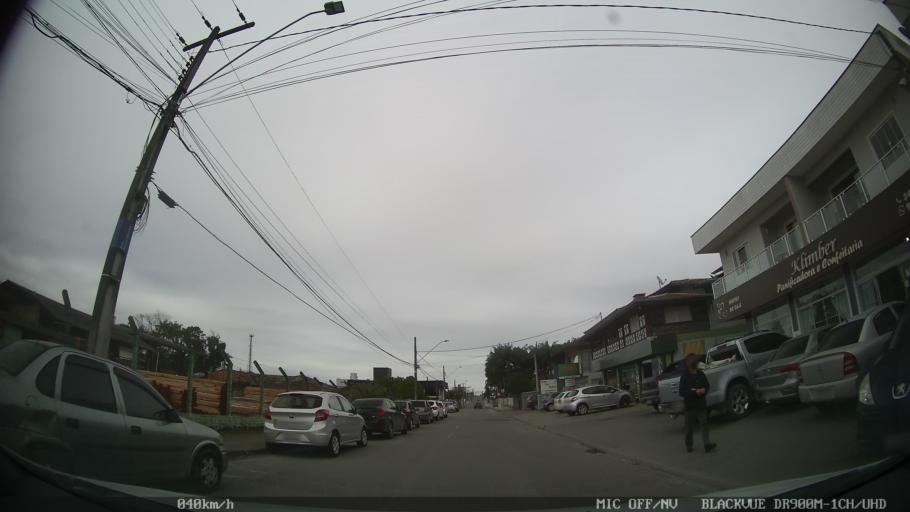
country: BR
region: Santa Catarina
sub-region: Joinville
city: Joinville
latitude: -26.2876
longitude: -48.9024
